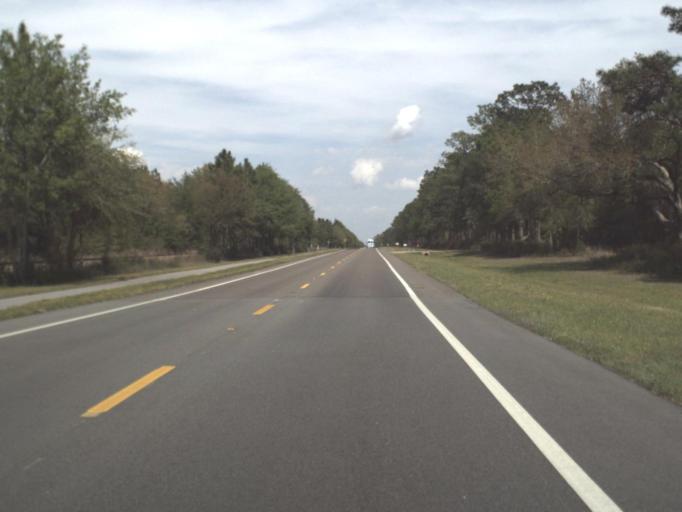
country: US
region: Florida
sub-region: Santa Rosa County
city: East Milton
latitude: 30.6443
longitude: -86.9315
